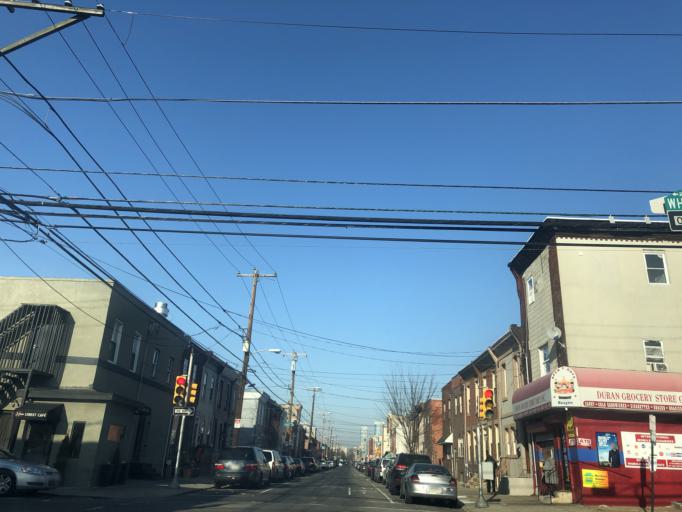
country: US
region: Pennsylvania
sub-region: Philadelphia County
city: Philadelphia
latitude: 39.9357
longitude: -75.1806
